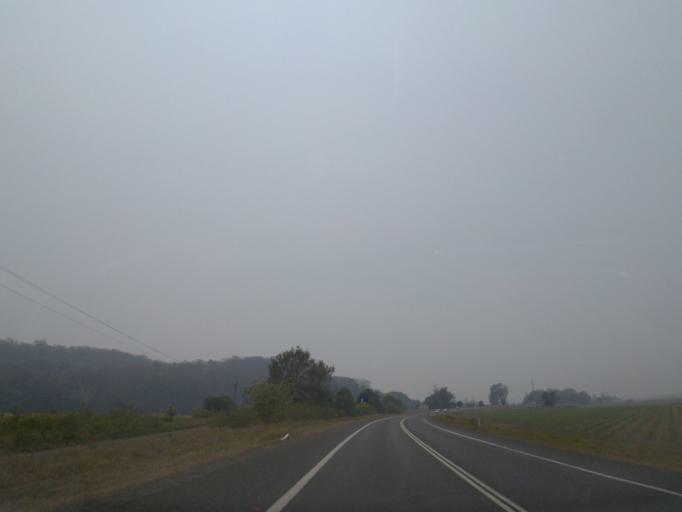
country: AU
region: New South Wales
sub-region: Clarence Valley
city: Maclean
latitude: -29.5416
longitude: 153.1584
